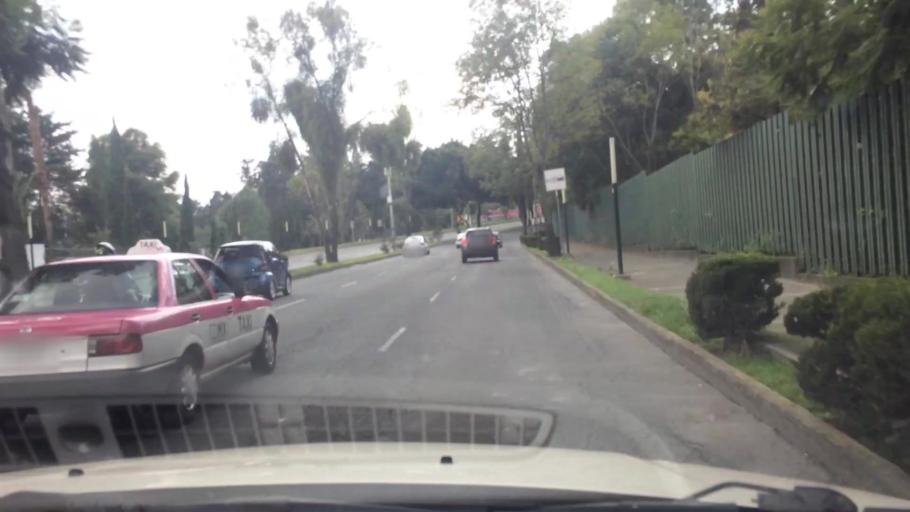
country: MX
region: Mexico City
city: Alvaro Obregon
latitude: 19.3520
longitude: -99.2046
